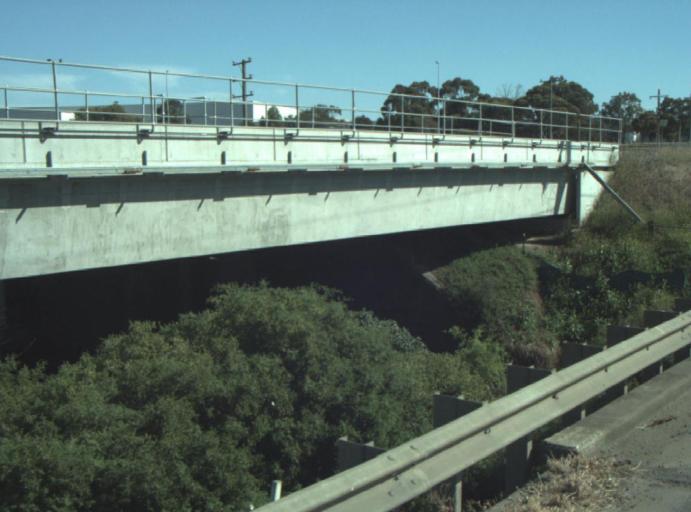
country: AU
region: Victoria
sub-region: Greater Geelong
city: Bell Park
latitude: -38.1061
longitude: 144.3584
